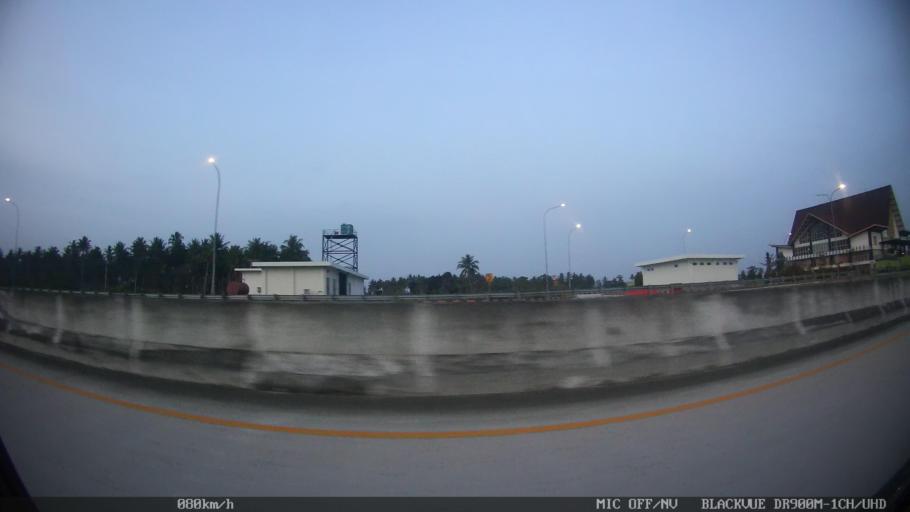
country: ID
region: Lampung
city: Kalianda
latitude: -5.6521
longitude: 105.5838
